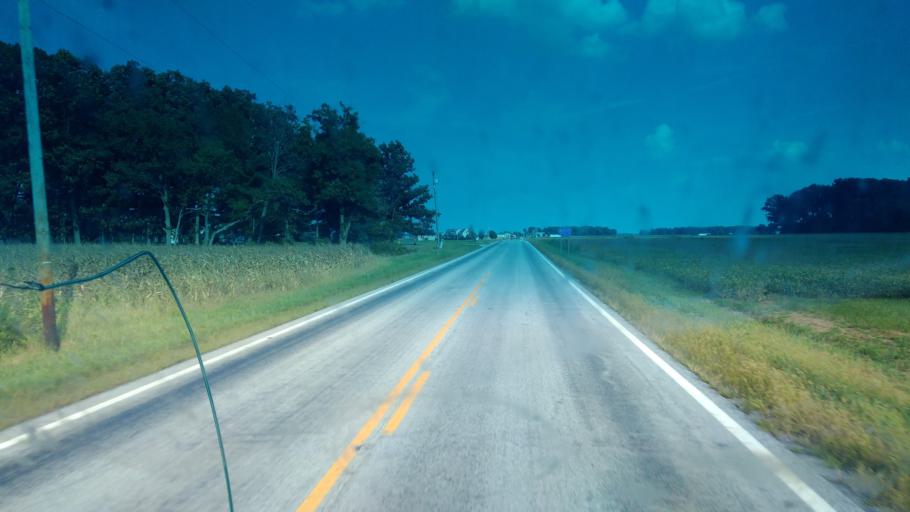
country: US
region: Ohio
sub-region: Hardin County
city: Forest
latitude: 40.8910
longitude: -83.5434
